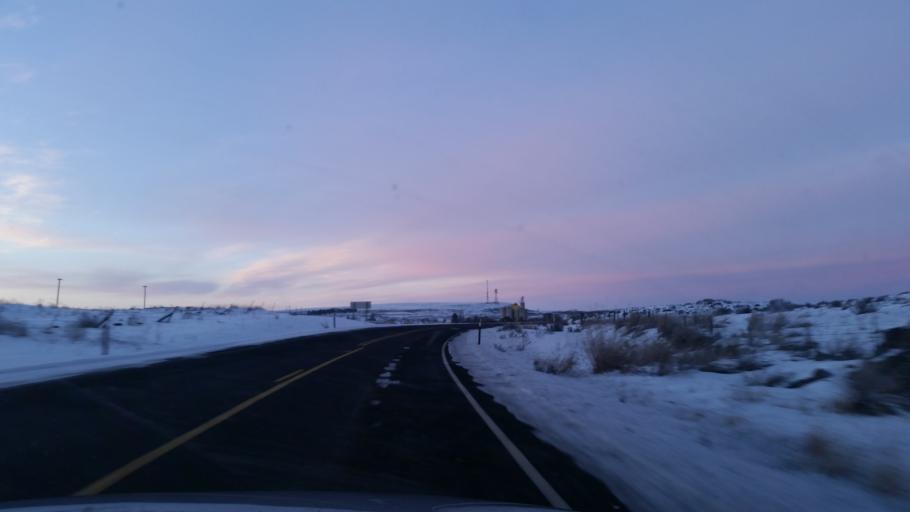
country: US
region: Washington
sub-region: Spokane County
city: Medical Lake
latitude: 47.2910
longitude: -117.9706
